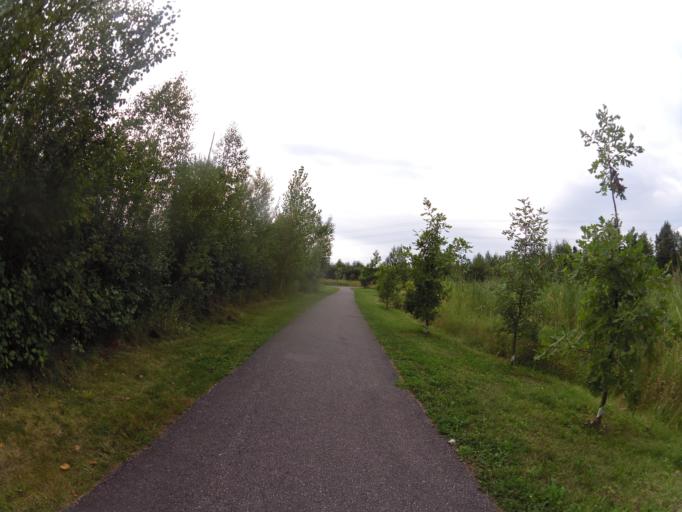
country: CA
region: Ontario
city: Bells Corners
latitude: 45.2787
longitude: -75.9352
